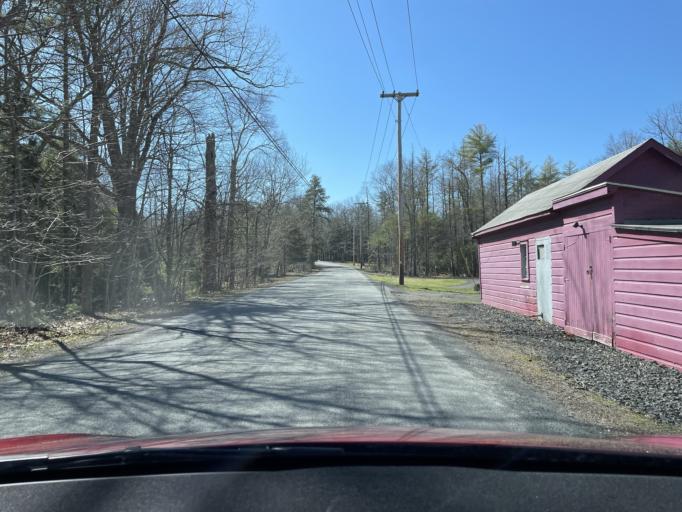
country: US
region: New York
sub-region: Ulster County
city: Manorville
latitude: 42.0745
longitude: -74.0241
